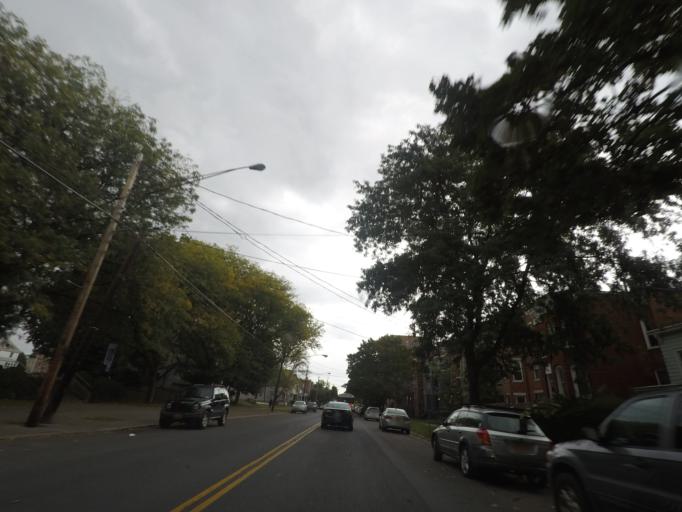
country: US
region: New York
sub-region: Albany County
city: West Albany
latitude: 42.6616
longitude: -73.7763
